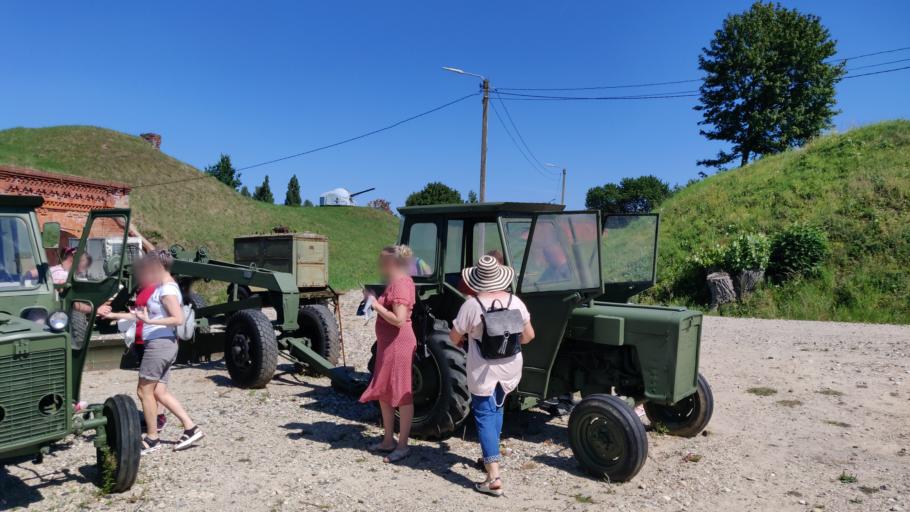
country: LT
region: Kauno apskritis
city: Dainava (Kaunas)
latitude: 54.9018
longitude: 23.9778
